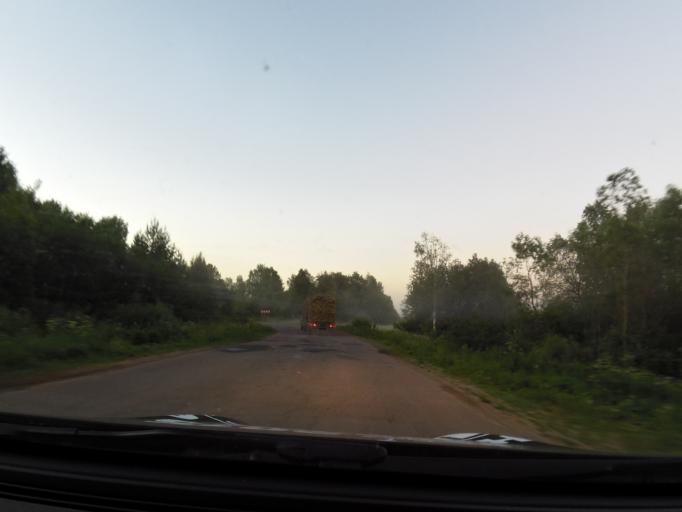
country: RU
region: Vologda
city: Vytegra
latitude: 60.8743
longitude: 36.0310
